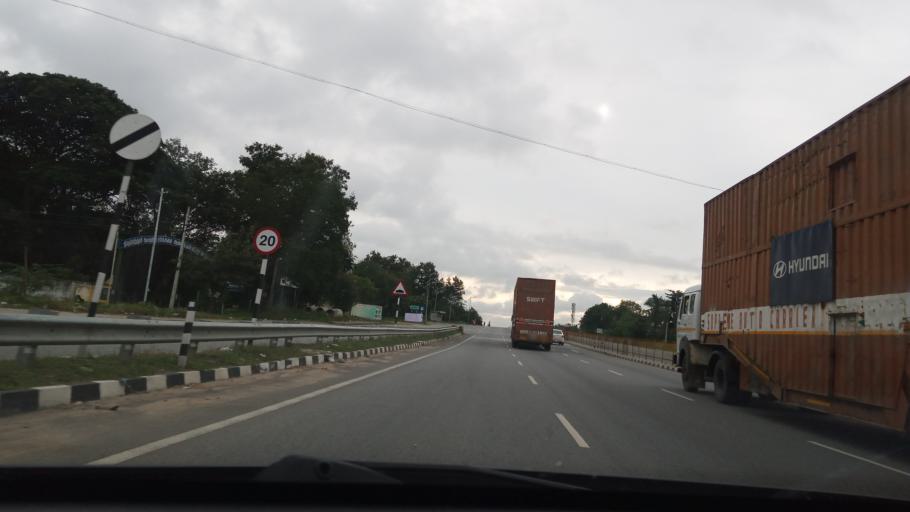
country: IN
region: Tamil Nadu
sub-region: Vellore
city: Jolarpettai
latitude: 12.6162
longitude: 78.5608
